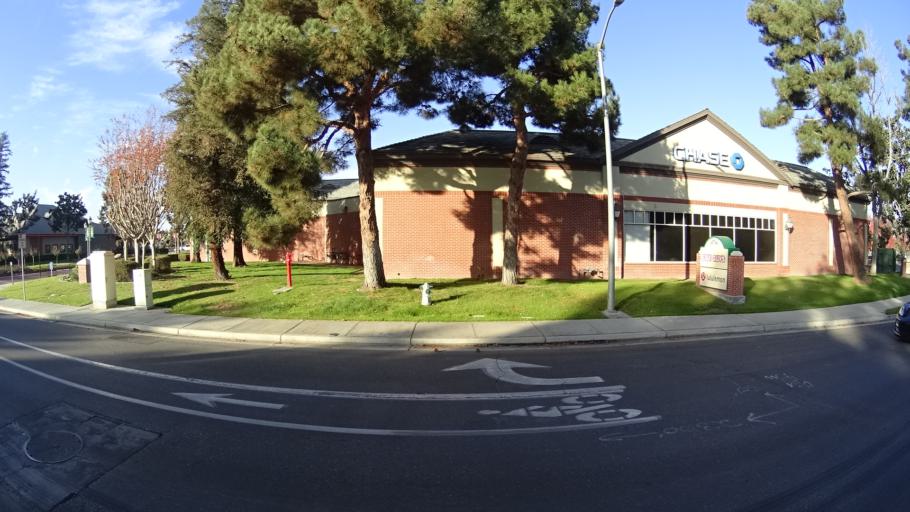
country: US
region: California
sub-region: Kern County
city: Greenacres
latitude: 35.3398
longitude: -119.1035
